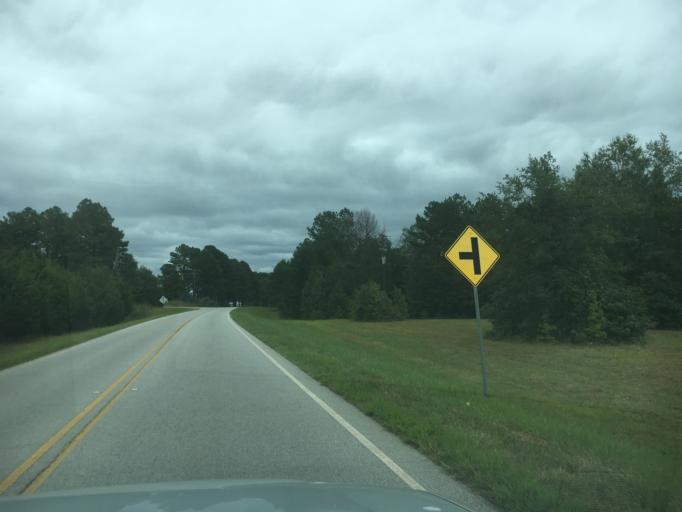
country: US
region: Georgia
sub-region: Lincoln County
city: Lincolnton
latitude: 33.7229
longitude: -82.5923
